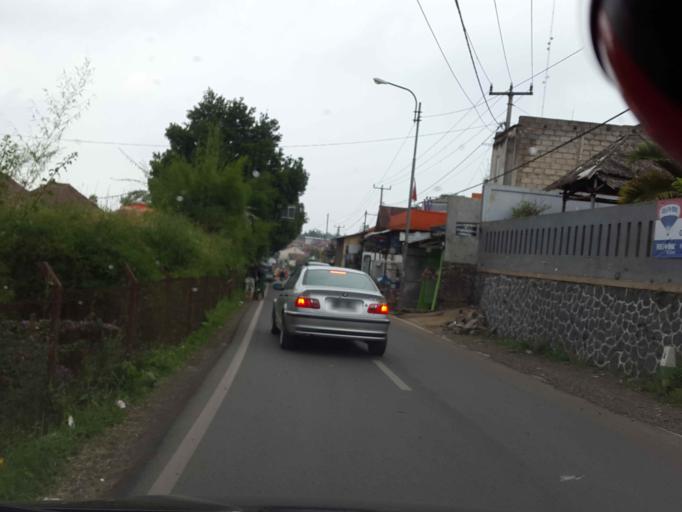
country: ID
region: West Java
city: Cimahi
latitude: -6.8166
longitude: 107.5546
